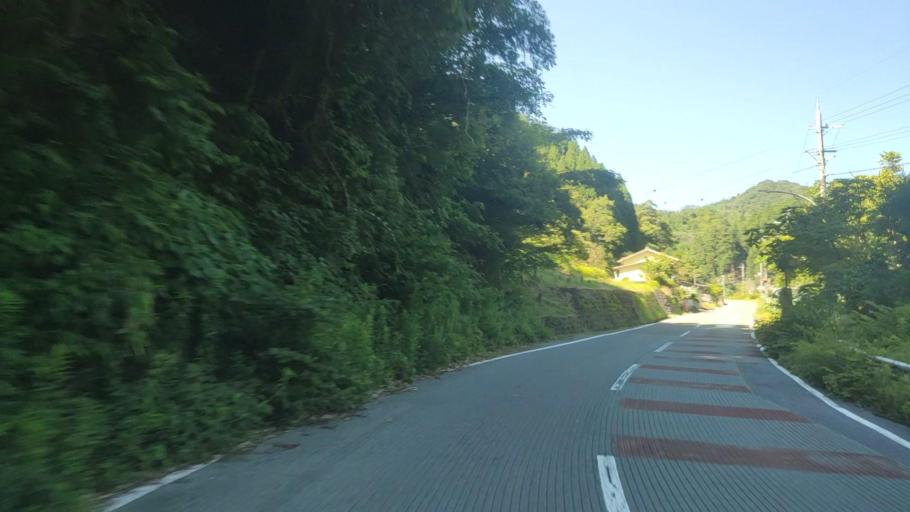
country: JP
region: Nara
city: Yoshino-cho
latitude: 34.4189
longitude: 135.9368
